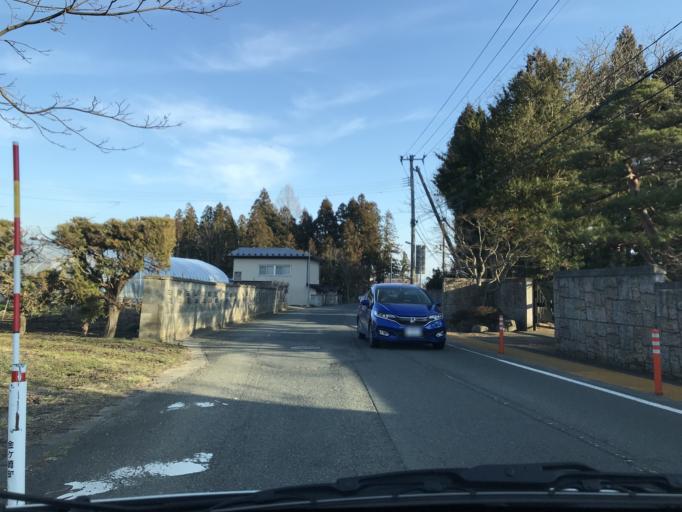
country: JP
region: Iwate
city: Kitakami
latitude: 39.2144
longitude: 141.1125
